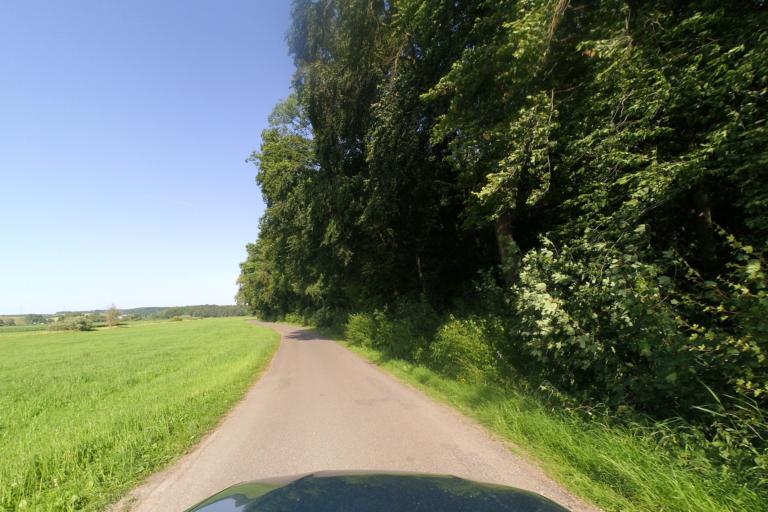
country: DE
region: Baden-Wuerttemberg
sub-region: Regierungsbezirk Stuttgart
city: Hermaringen
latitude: 48.5810
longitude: 10.2481
